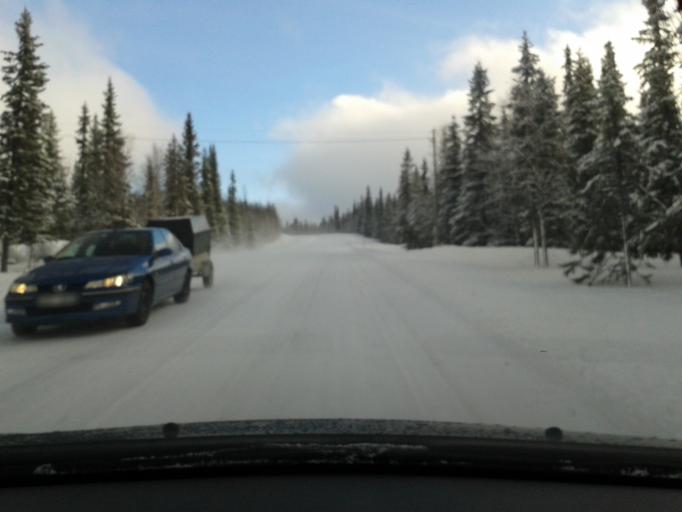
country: SE
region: Vaesterbotten
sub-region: Vilhelmina Kommun
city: Sjoberg
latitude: 65.2511
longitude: 15.6291
